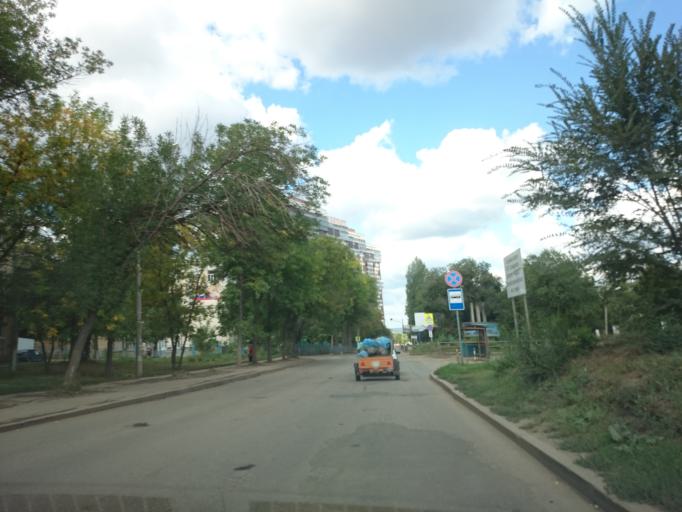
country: RU
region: Samara
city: Samara
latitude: 53.2351
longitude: 50.1850
